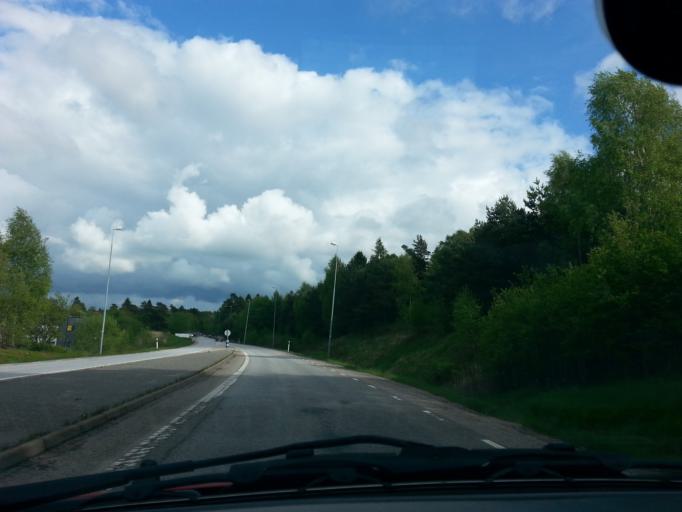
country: SE
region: Vaestra Goetaland
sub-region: Partille Kommun
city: Furulund
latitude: 57.7233
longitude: 12.1302
